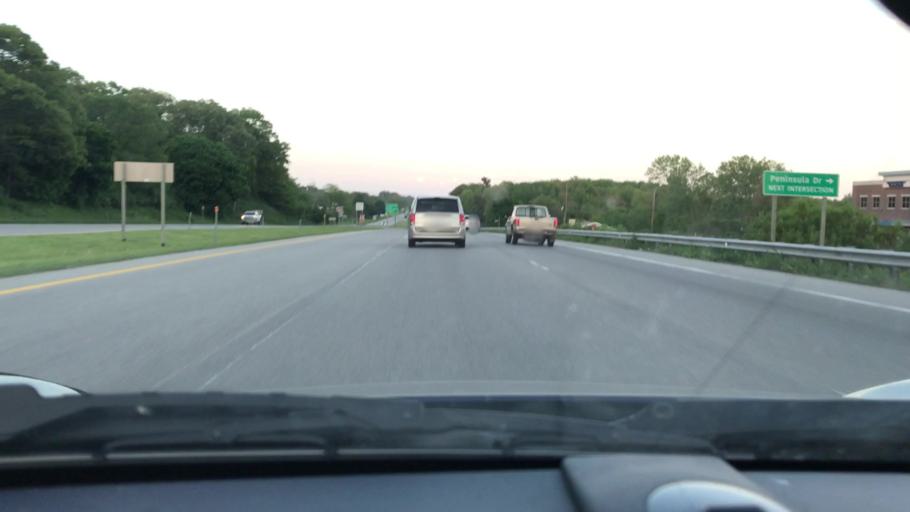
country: US
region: Michigan
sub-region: Muskegon County
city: Muskegon Heights
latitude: 43.1893
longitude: -86.2499
